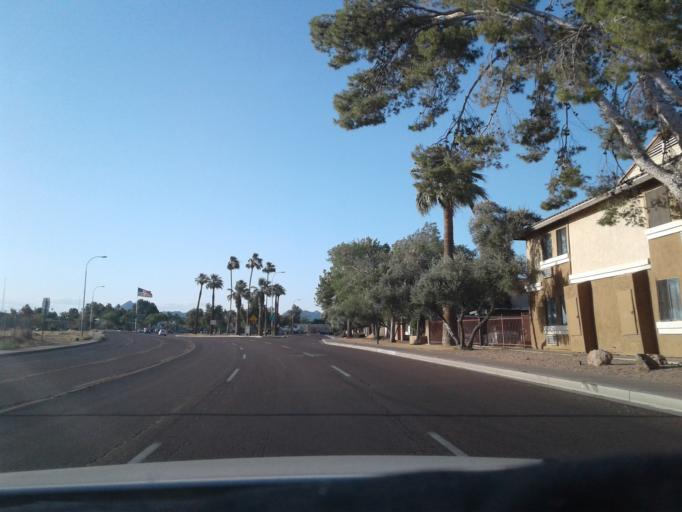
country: US
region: Arizona
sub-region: Maricopa County
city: Tempe Junction
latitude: 33.4629
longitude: -111.9950
